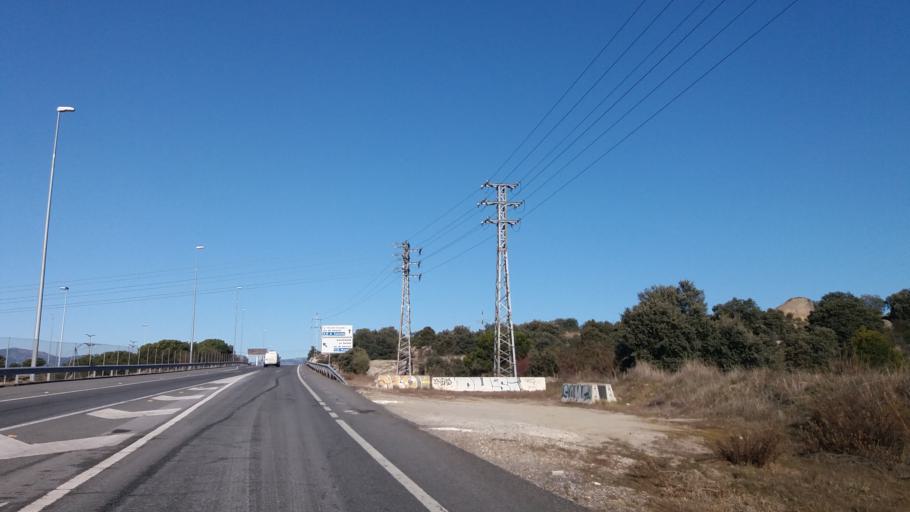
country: ES
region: Madrid
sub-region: Provincia de Madrid
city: Collado-Villalba
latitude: 40.6116
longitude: -3.9770
